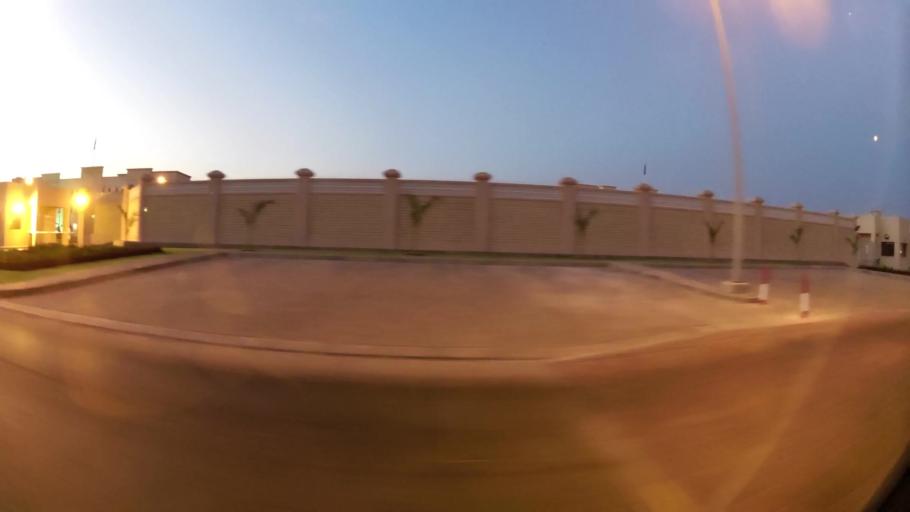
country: OM
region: Muhafazat Masqat
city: As Sib al Jadidah
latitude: 23.6639
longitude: 58.1859
